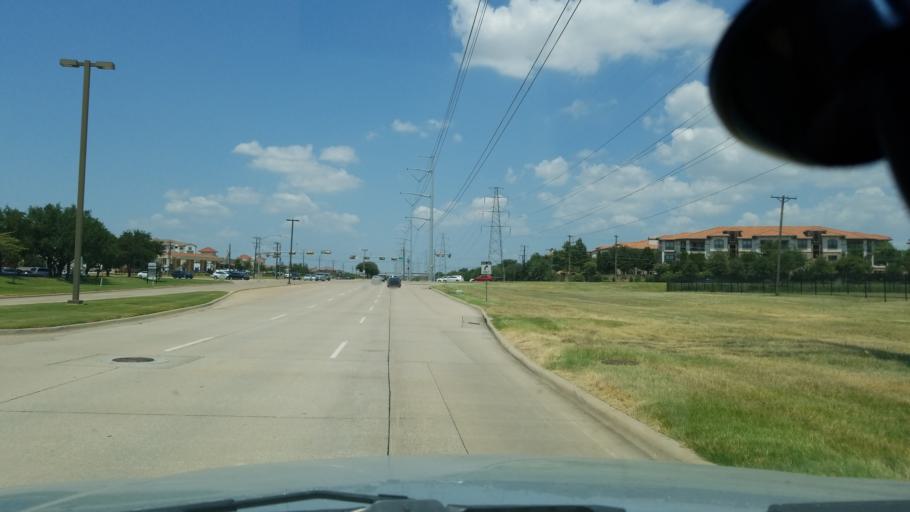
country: US
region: Texas
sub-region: Dallas County
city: Farmers Branch
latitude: 32.8943
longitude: -96.9375
